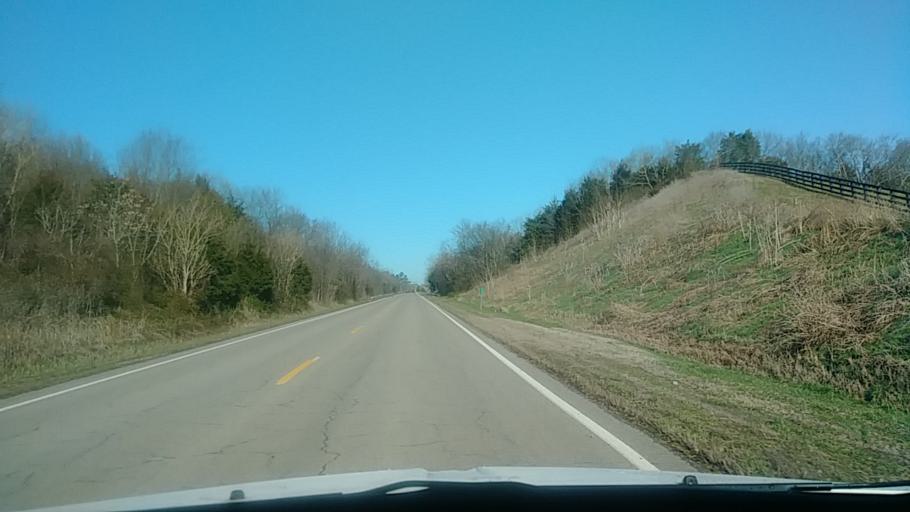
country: US
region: Tennessee
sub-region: Hamblen County
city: Morristown
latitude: 36.1786
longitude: -83.1621
